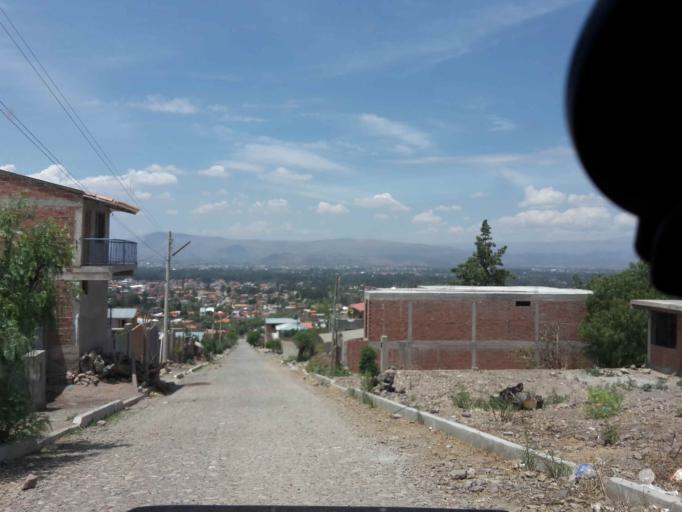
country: BO
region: Cochabamba
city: Cochabamba
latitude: -17.3204
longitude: -66.2226
